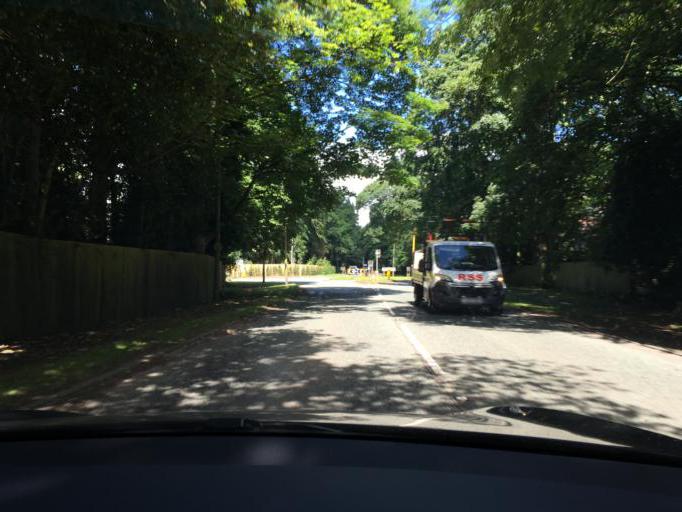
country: GB
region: England
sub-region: Cheshire East
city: Knutsford
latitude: 53.2937
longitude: -2.3543
